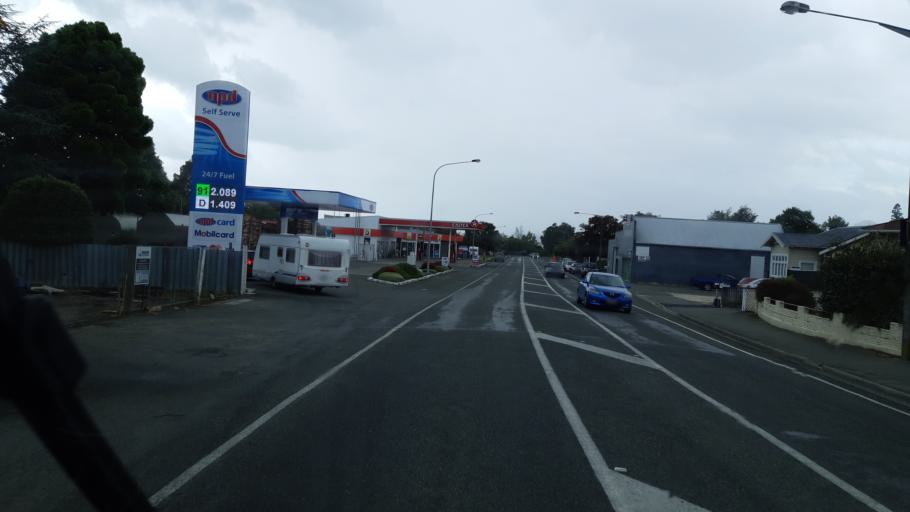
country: NZ
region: Tasman
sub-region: Tasman District
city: Wakefield
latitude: -41.4047
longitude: 173.0443
